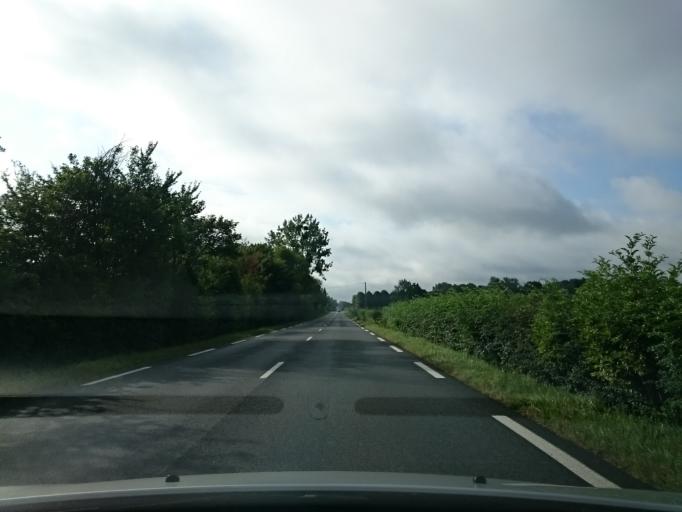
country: FR
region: Lower Normandy
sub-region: Departement du Calvados
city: Cambremer
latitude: 49.1290
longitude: 0.0034
